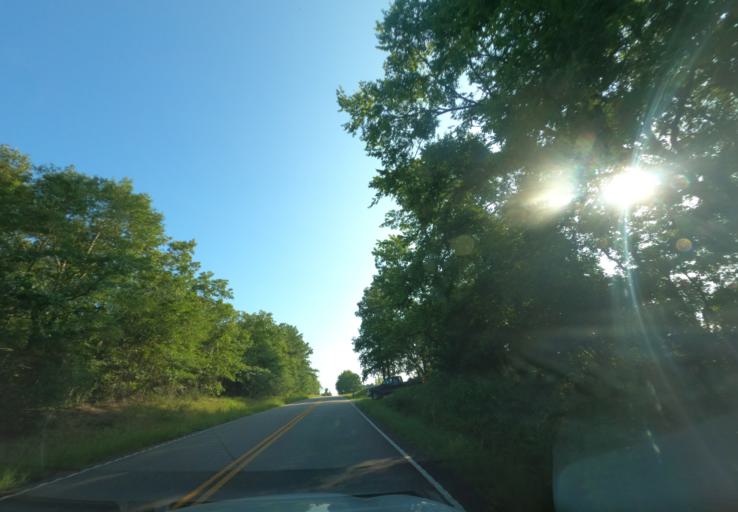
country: US
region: South Carolina
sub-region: Edgefield County
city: Murphys Estates
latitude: 33.5975
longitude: -81.9778
